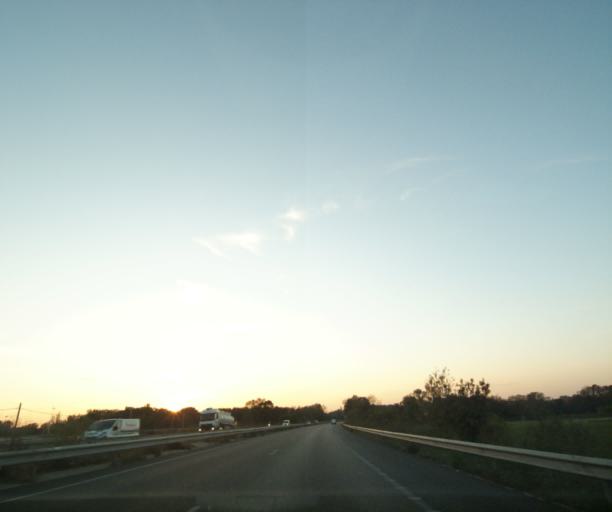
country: FR
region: Provence-Alpes-Cote d'Azur
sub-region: Departement des Bouches-du-Rhone
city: Saint-Martin-de-Crau
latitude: 43.6295
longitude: 4.7590
